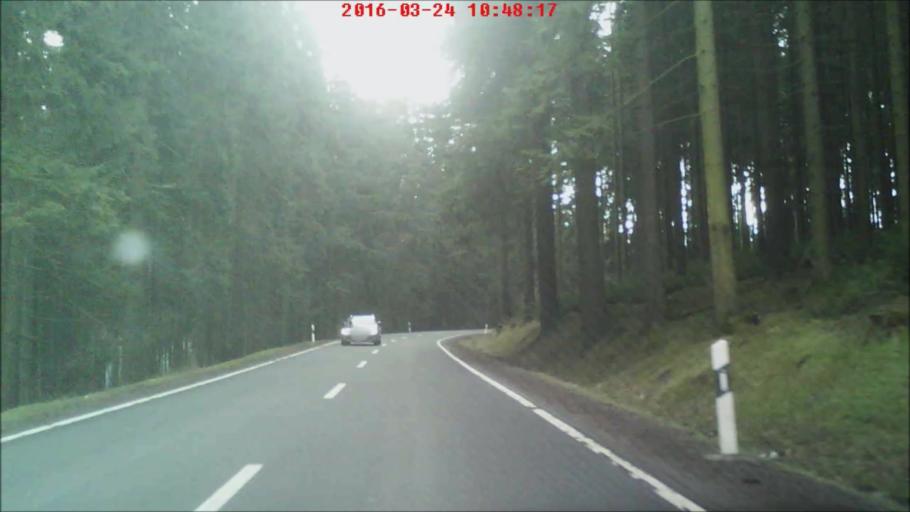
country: DE
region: Thuringia
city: Mohrenbach
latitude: 50.6079
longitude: 10.9819
